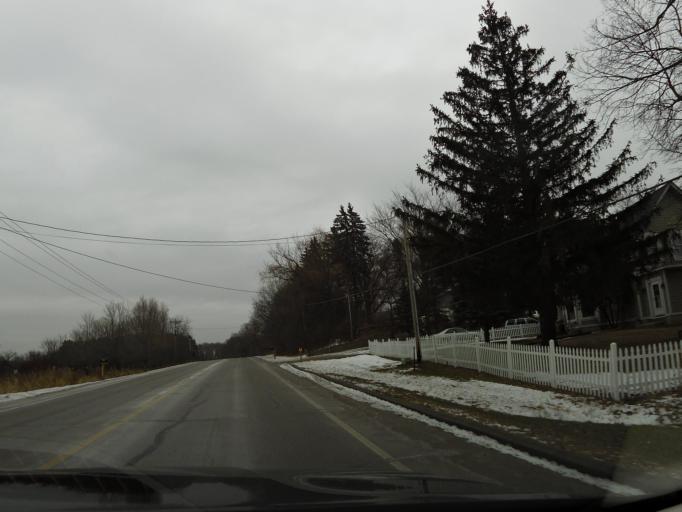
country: US
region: Minnesota
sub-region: Hennepin County
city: Orono
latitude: 44.9971
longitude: -93.6059
